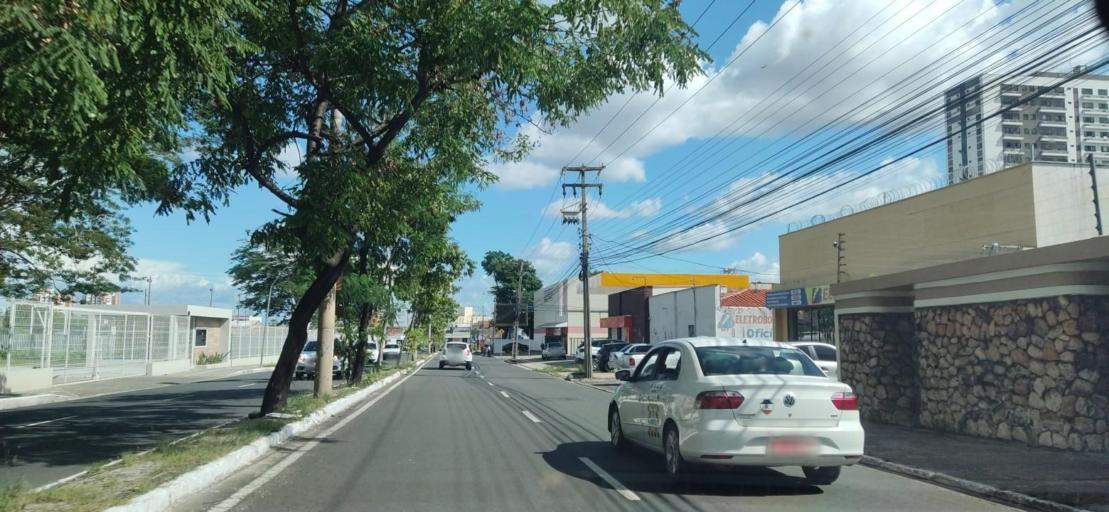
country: BR
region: Piaui
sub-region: Teresina
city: Teresina
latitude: -5.0779
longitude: -42.7904
